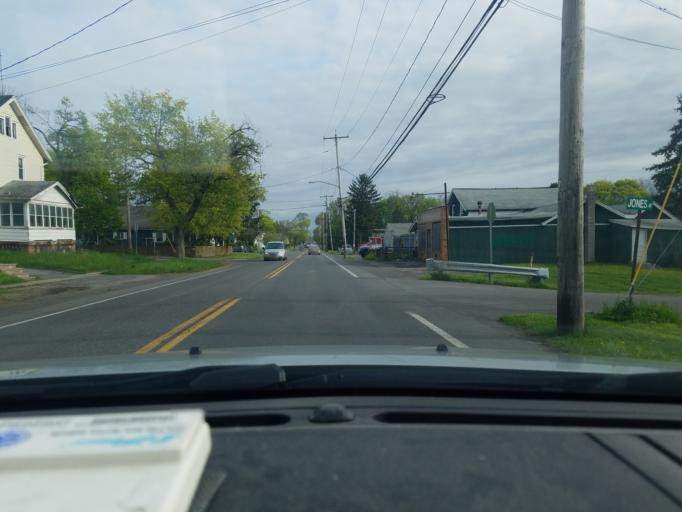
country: US
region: New York
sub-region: Onondaga County
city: East Syracuse
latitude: 43.0715
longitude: -76.0770
